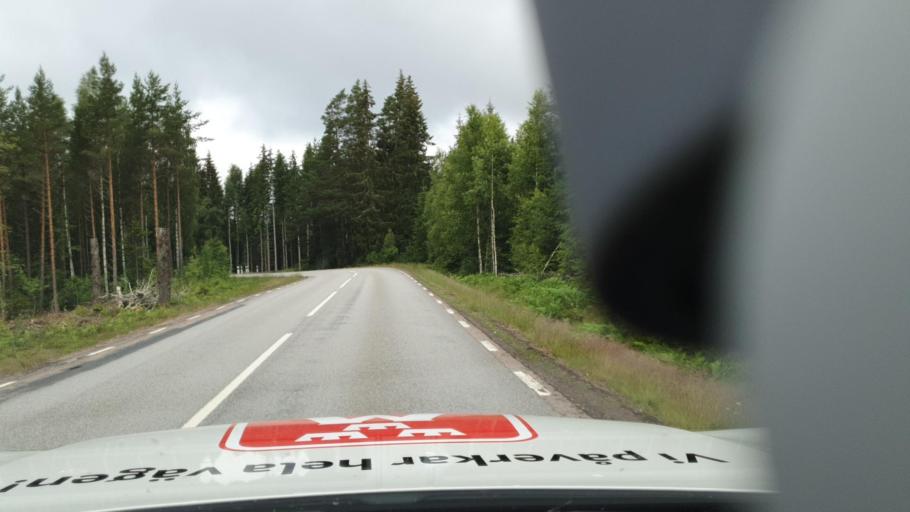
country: SE
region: Vaermland
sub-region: Kristinehamns Kommun
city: Bjorneborg
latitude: 59.1161
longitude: 14.2141
